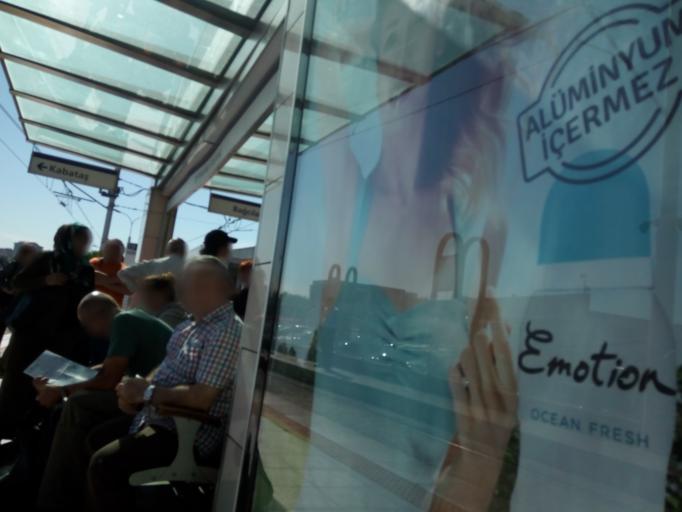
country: TR
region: Istanbul
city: guengoeren merter
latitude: 41.0015
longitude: 28.8901
